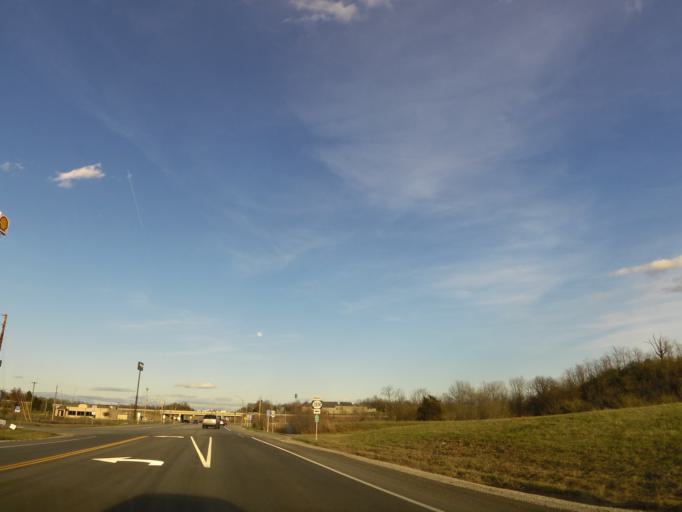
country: US
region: Kentucky
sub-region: Madison County
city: Berea
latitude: 37.5965
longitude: -84.3184
